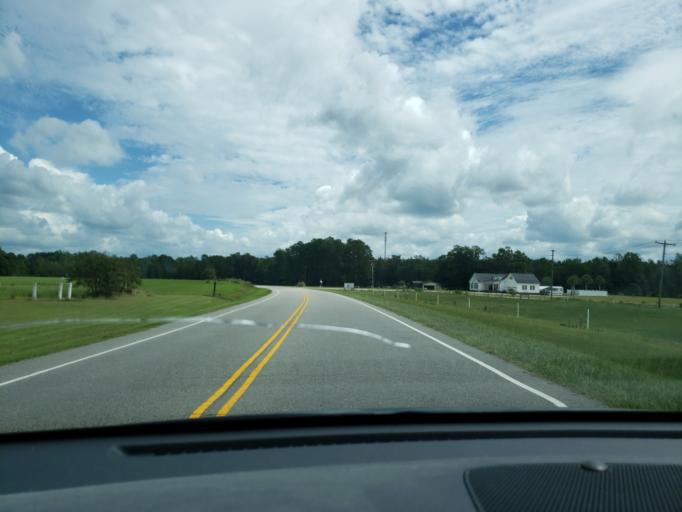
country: US
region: North Carolina
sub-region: Columbus County
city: Tabor City
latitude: 34.1880
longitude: -78.7774
